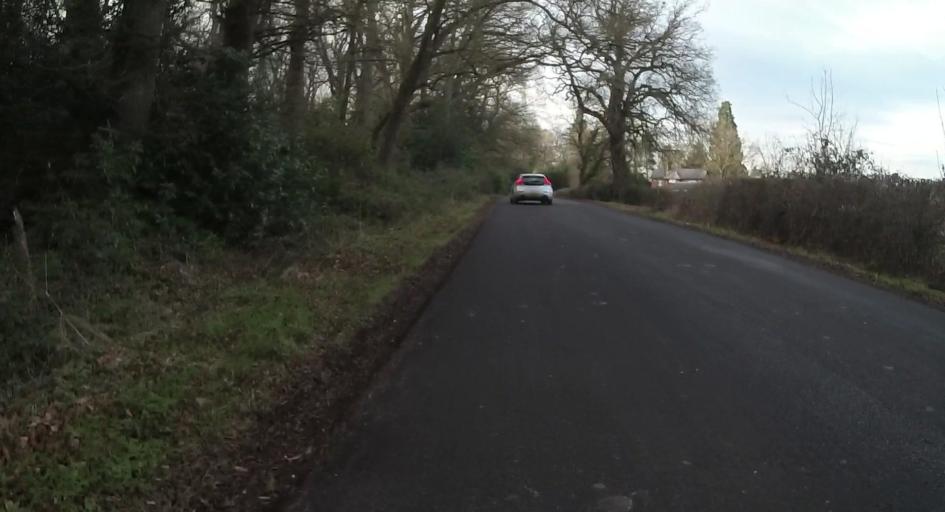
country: GB
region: England
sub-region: West Berkshire
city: Stratfield Mortimer
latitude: 51.4058
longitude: -1.0420
